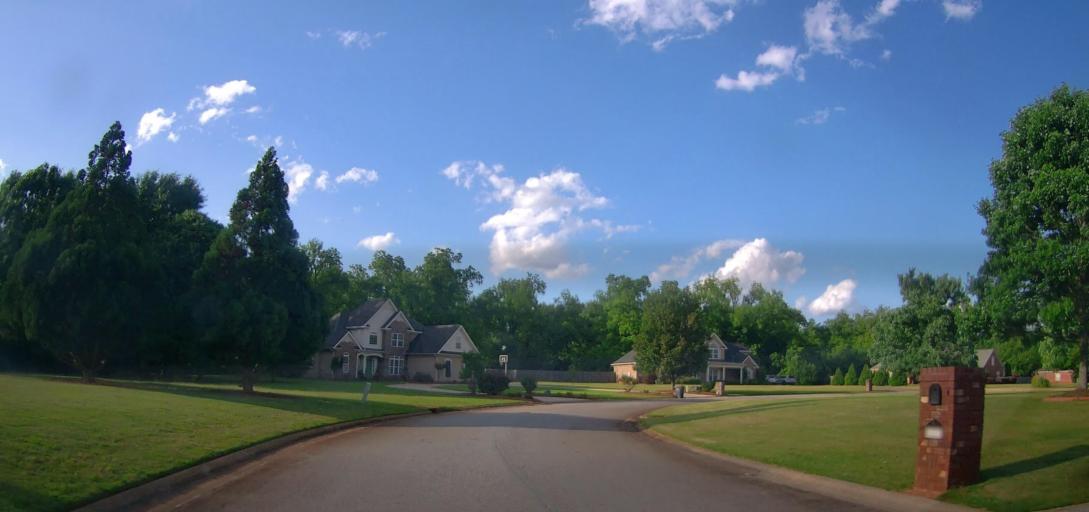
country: US
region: Georgia
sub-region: Peach County
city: Byron
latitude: 32.6502
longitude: -83.7945
